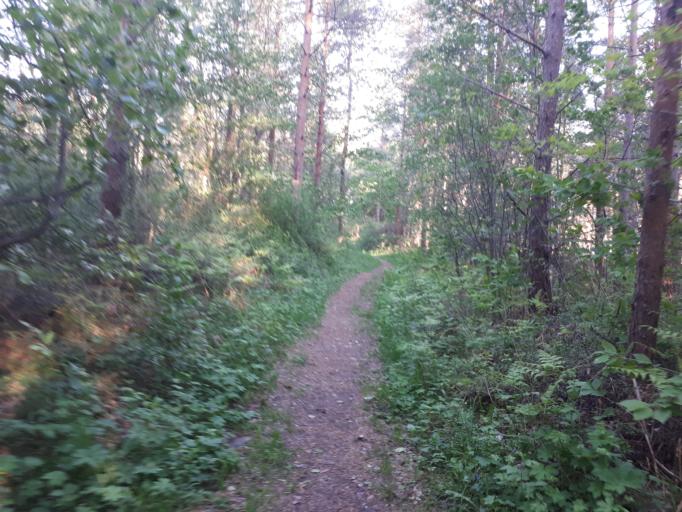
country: SE
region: Gotland
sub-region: Gotland
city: Visby
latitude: 57.6028
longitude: 18.3001
